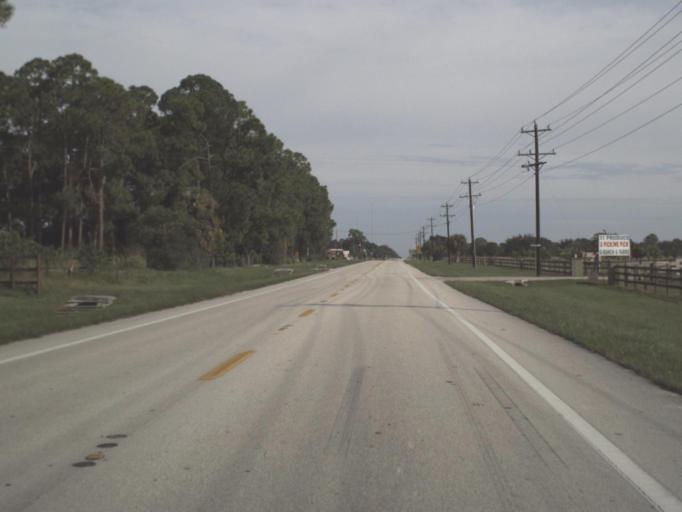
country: US
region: Florida
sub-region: Lee County
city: Fort Myers Shores
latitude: 26.7345
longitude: -81.7610
